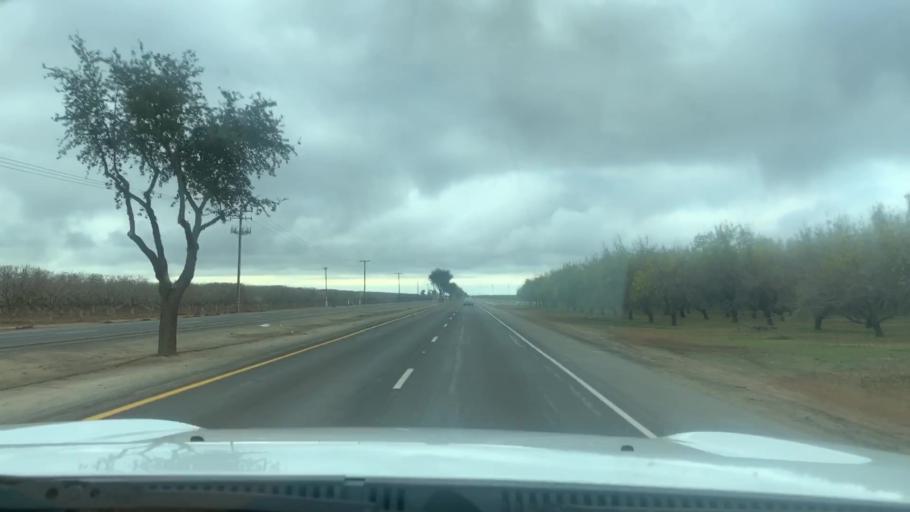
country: US
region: California
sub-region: Kern County
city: Shafter
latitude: 35.4998
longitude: -119.2126
